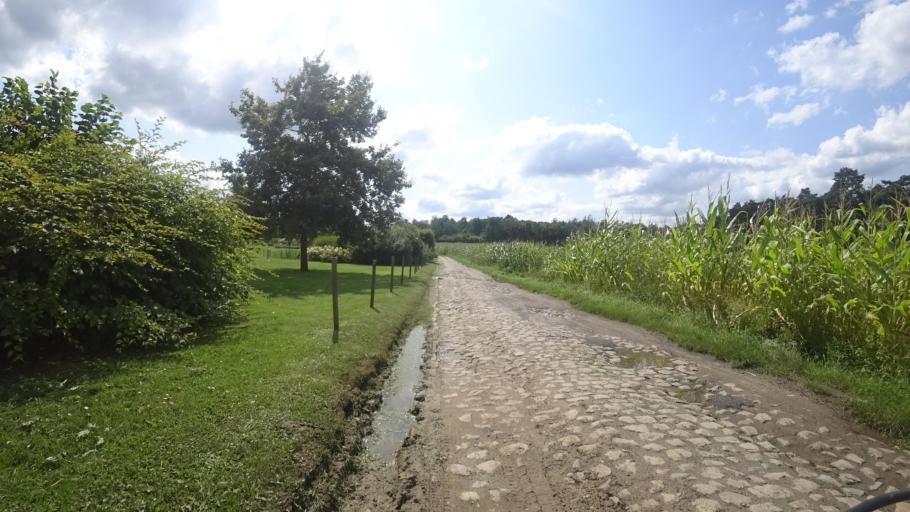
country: BE
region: Wallonia
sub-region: Province du Brabant Wallon
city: Grez-Doiceau
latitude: 50.7446
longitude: 4.6655
